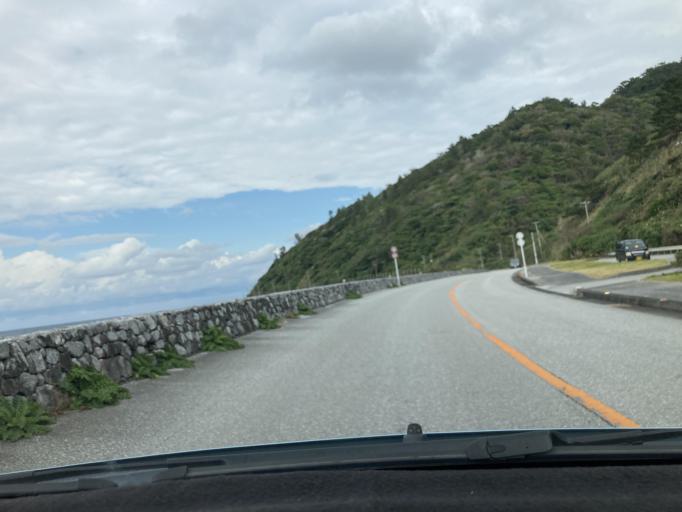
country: JP
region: Okinawa
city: Nago
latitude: 26.7680
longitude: 128.2045
